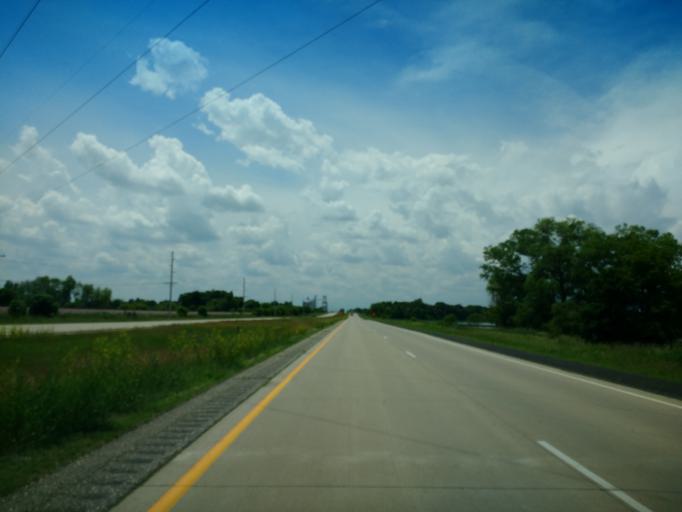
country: US
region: Minnesota
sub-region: Jackson County
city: Lakefield
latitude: 43.8065
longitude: -95.3055
